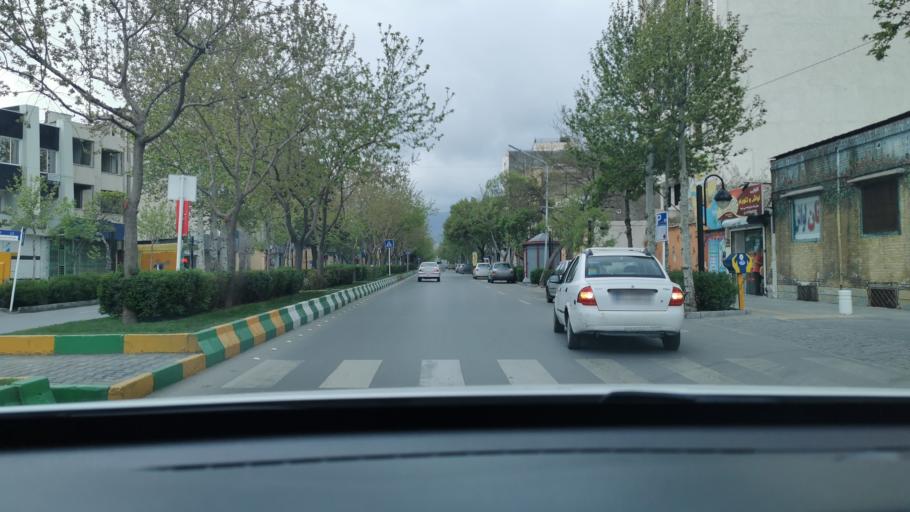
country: IR
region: Razavi Khorasan
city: Mashhad
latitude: 36.2798
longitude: 59.5949
